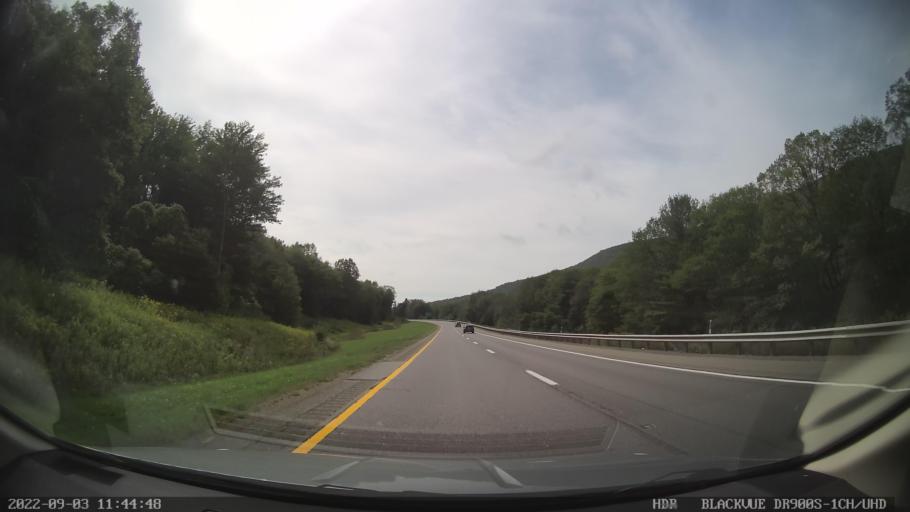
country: US
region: Pennsylvania
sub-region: Tioga County
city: Mansfield
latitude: 41.8608
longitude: -77.1123
